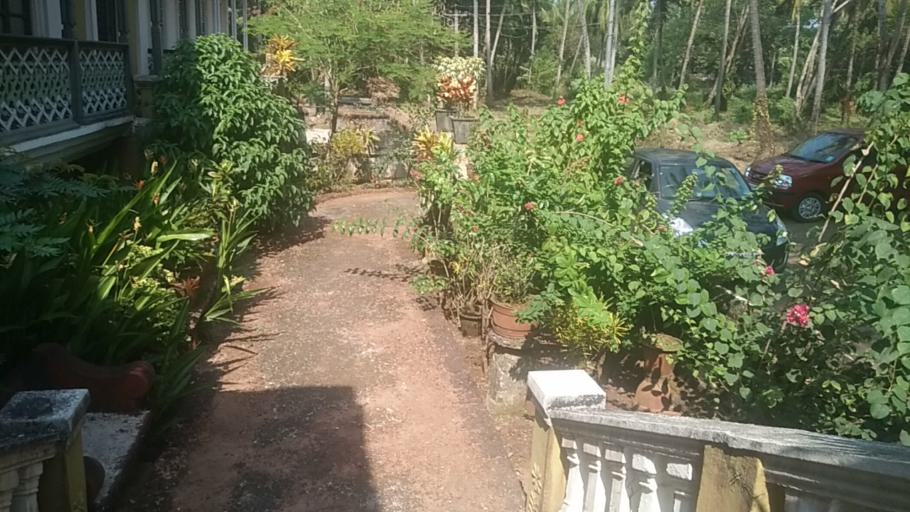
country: IN
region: Goa
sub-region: South Goa
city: Sancoale
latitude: 15.3502
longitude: 73.8921
